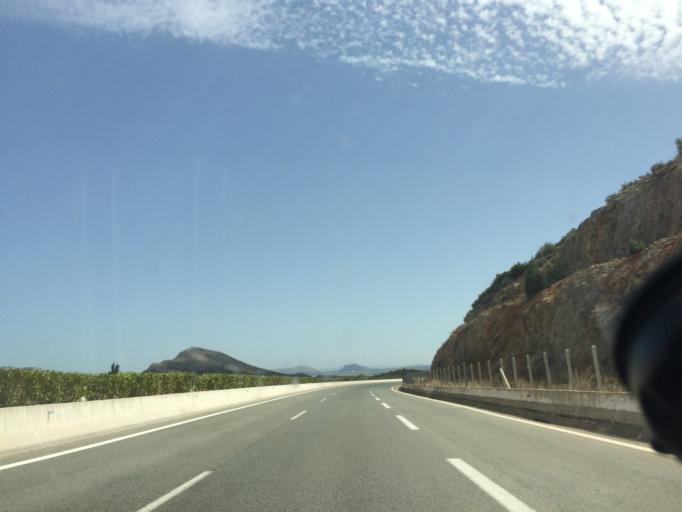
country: GR
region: Central Greece
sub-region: Nomos Voiotias
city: Akraifnia
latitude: 38.4010
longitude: 23.2251
